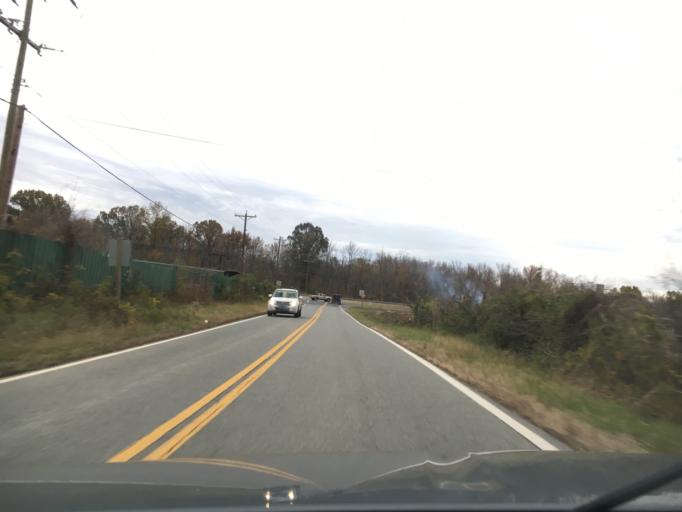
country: US
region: Virginia
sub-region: Halifax County
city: South Boston
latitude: 36.6834
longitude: -78.9068
